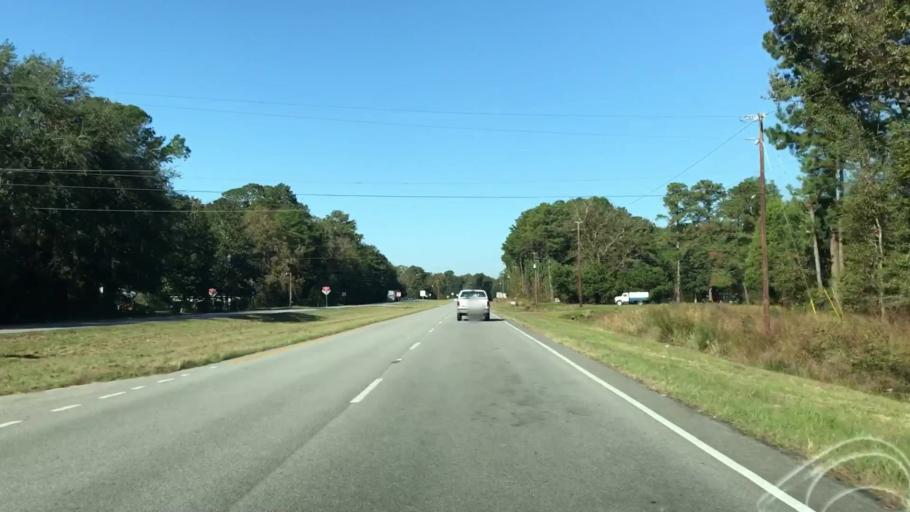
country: US
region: South Carolina
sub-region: Hampton County
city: Yemassee
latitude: 32.6034
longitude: -80.8014
